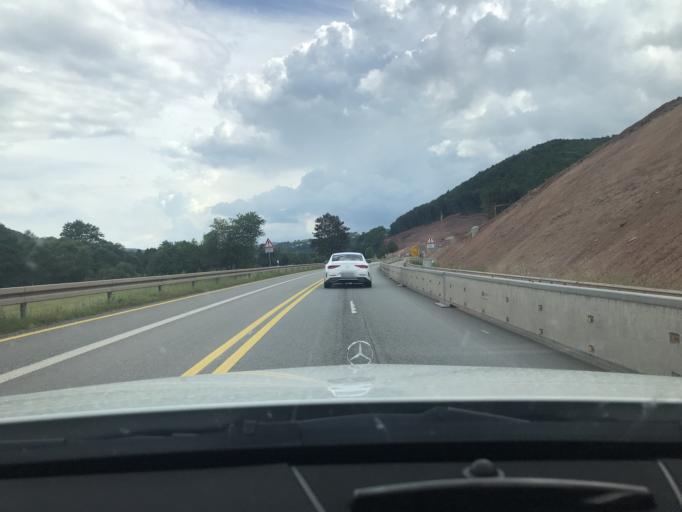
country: DE
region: Hesse
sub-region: Regierungsbezirk Kassel
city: Sontra
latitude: 51.0923
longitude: 9.9458
